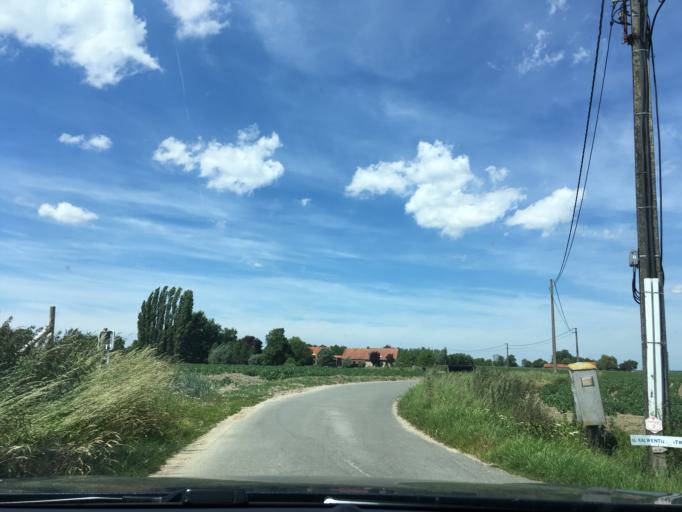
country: BE
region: Flanders
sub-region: Provincie West-Vlaanderen
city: Lichtervelde
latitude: 51.0263
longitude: 3.1711
